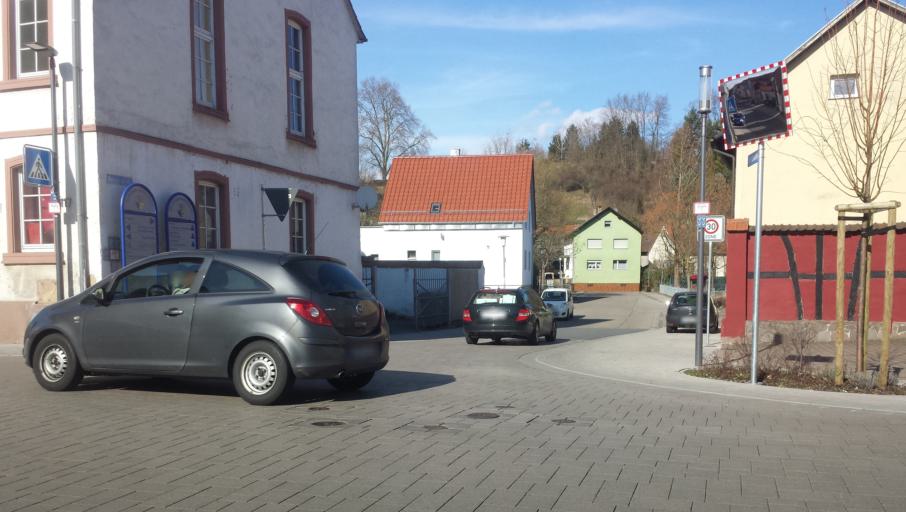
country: DE
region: Baden-Wuerttemberg
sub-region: Karlsruhe Region
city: Muhlhausen
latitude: 49.2477
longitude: 8.7305
